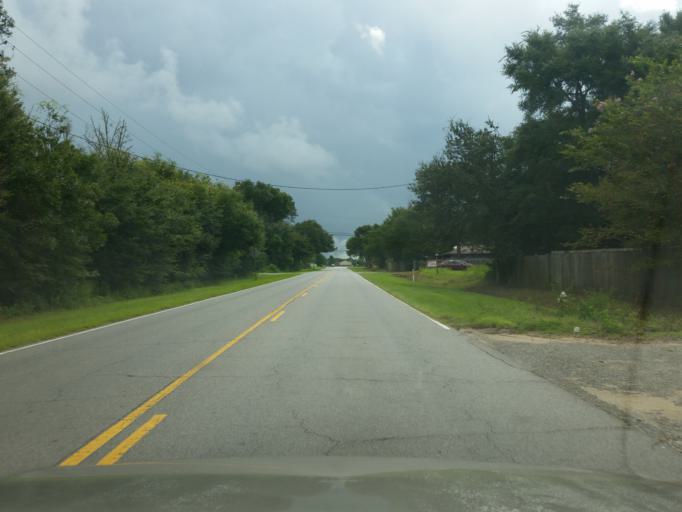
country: US
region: Florida
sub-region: Escambia County
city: West Pensacola
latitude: 30.4468
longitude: -87.2851
